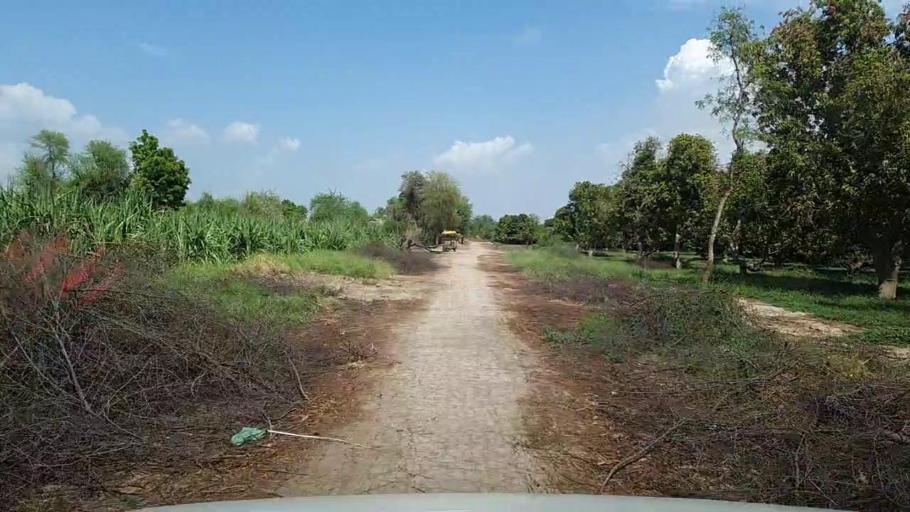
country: PK
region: Sindh
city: Bhiria
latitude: 26.9213
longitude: 68.2214
